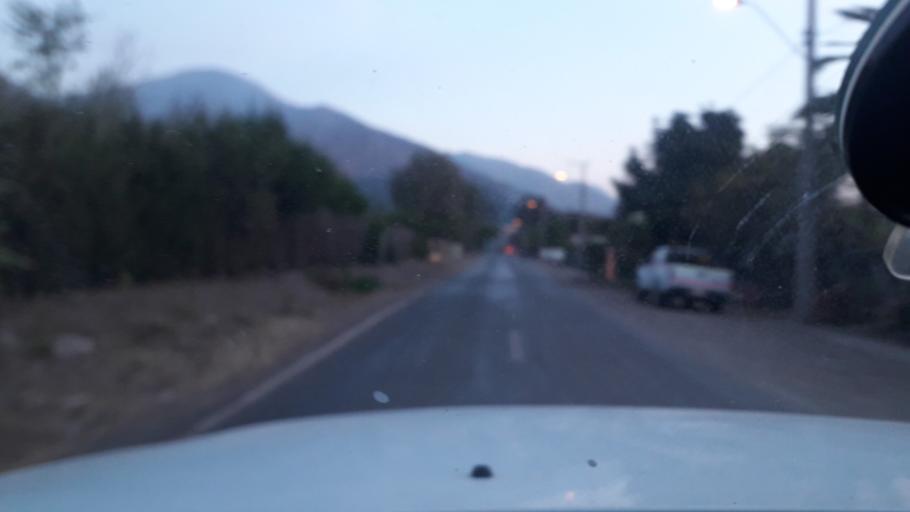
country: CL
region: Valparaiso
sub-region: Provincia de San Felipe
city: Llaillay
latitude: -32.8244
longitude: -71.0295
